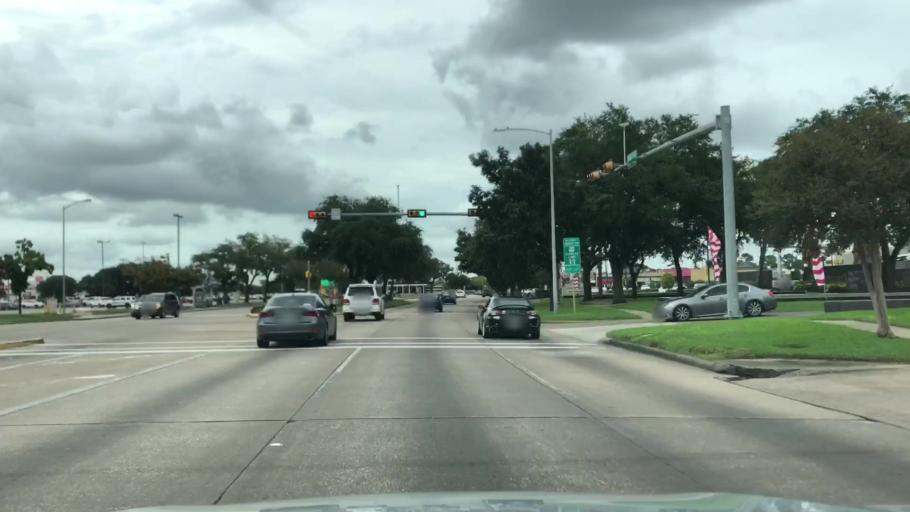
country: US
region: Texas
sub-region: Harris County
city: Piney Point Village
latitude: 29.7051
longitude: -95.5172
